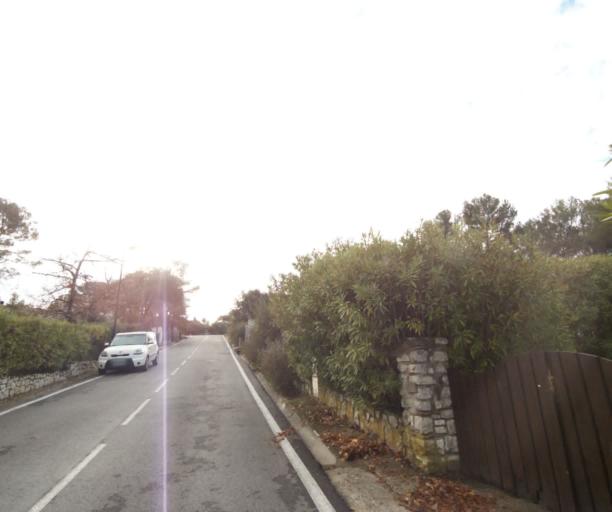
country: FR
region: Provence-Alpes-Cote d'Azur
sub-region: Departement du Var
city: Trans-en-Provence
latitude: 43.4915
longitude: 6.4968
